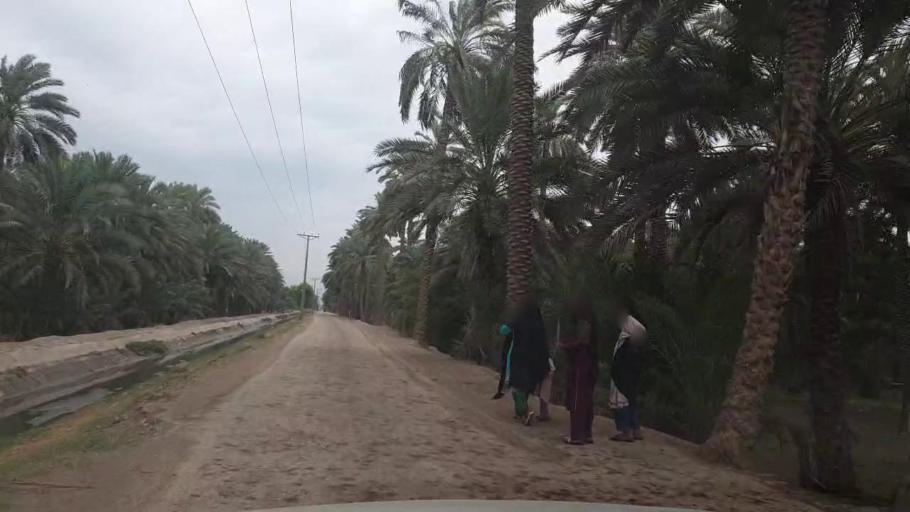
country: PK
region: Sindh
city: Sukkur
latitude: 27.6195
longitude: 68.8191
